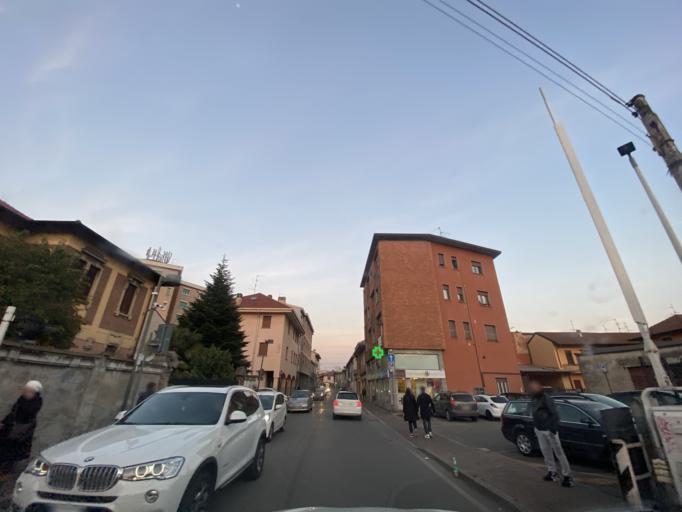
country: IT
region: Lombardy
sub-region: Provincia di Monza e Brianza
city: Varedo
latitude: 45.5970
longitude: 9.1526
